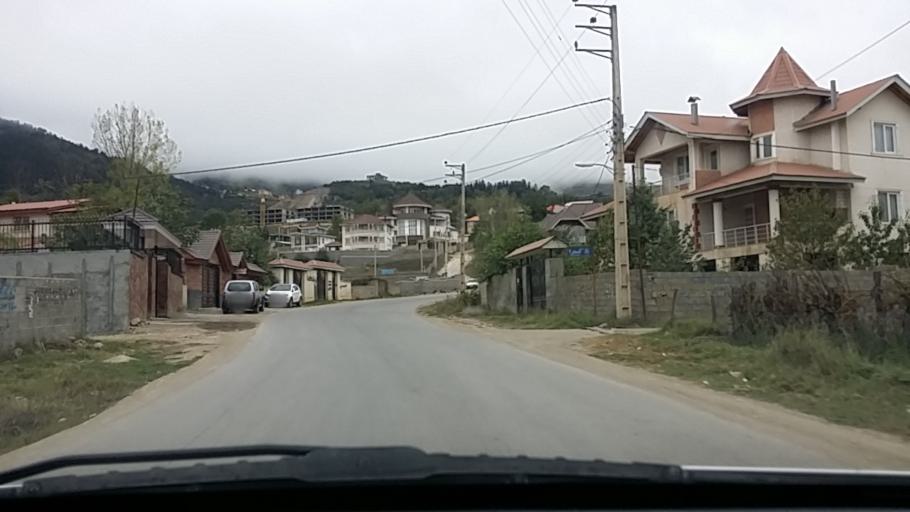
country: IR
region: Mazandaran
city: `Abbasabad
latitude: 36.4992
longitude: 51.1564
